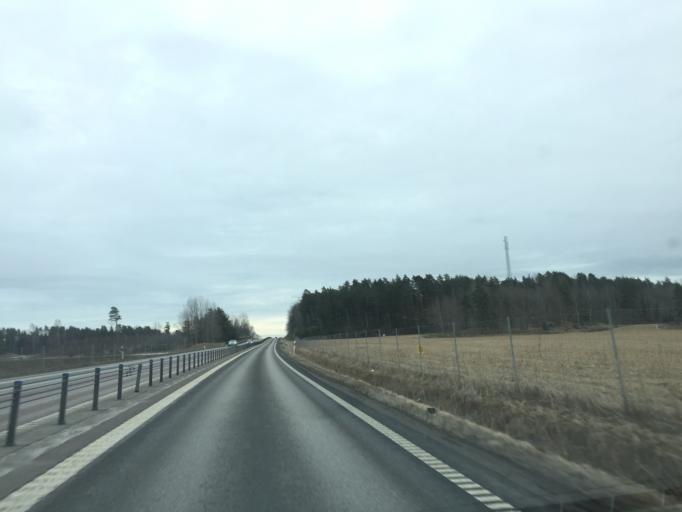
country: SE
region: Vaestmanland
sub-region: Kopings Kommun
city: Koping
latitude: 59.5513
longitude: 16.0255
